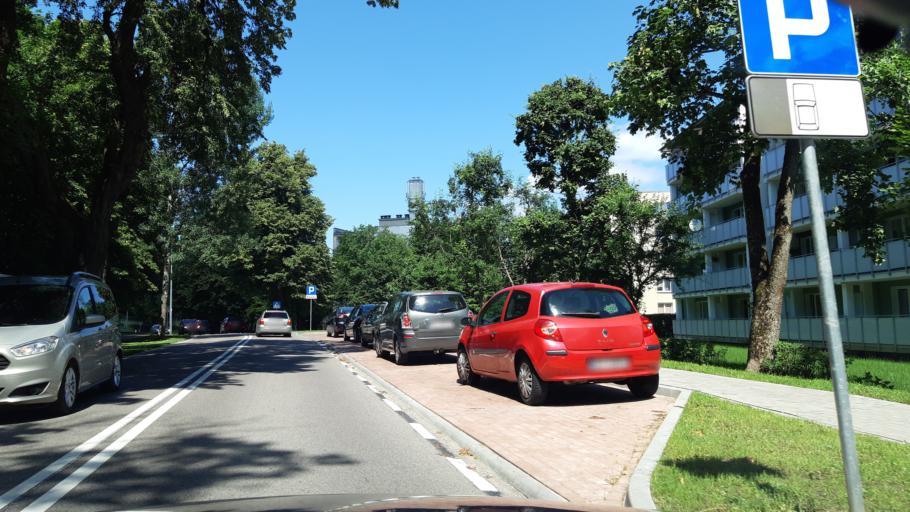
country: PL
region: Warmian-Masurian Voivodeship
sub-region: Powiat gizycki
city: Gizycko
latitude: 54.0360
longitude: 21.7531
